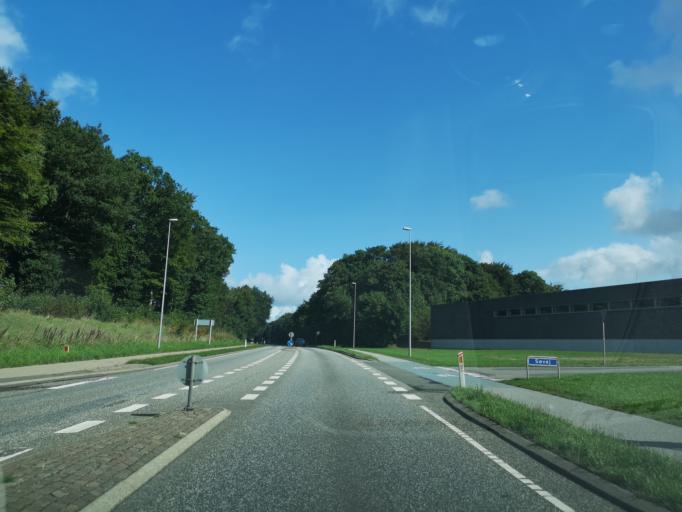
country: DK
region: Central Jutland
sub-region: Holstebro Kommune
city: Holstebro
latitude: 56.3535
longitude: 8.6395
